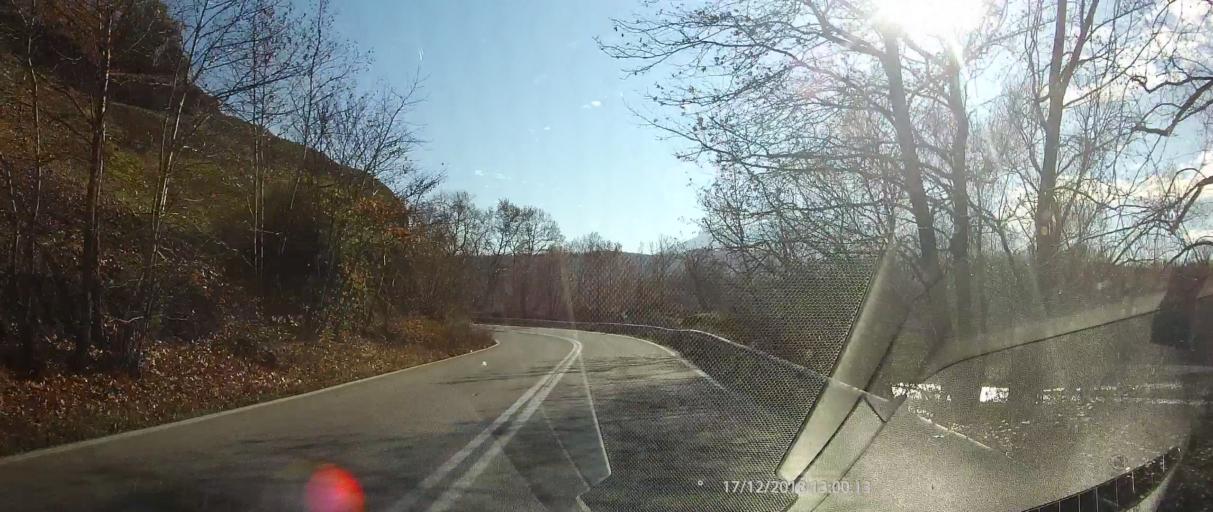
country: GR
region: Thessaly
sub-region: Trikala
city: Kastraki
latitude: 39.7299
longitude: 21.5651
